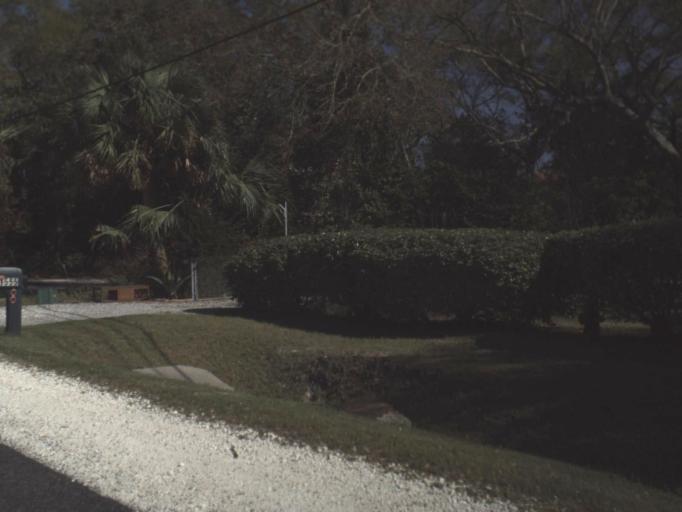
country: US
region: Florida
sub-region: Okaloosa County
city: Mary Esther
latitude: 30.4118
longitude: -86.7244
